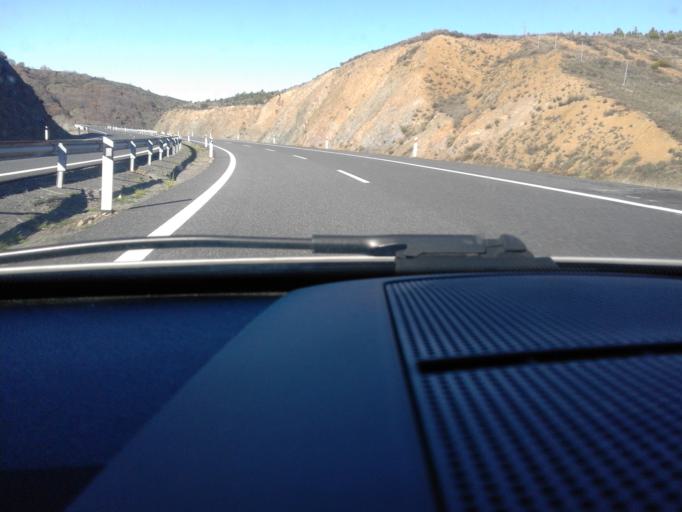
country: ES
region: Castille and Leon
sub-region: Provincia de Leon
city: Carrocera
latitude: 42.7670
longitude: -5.7771
